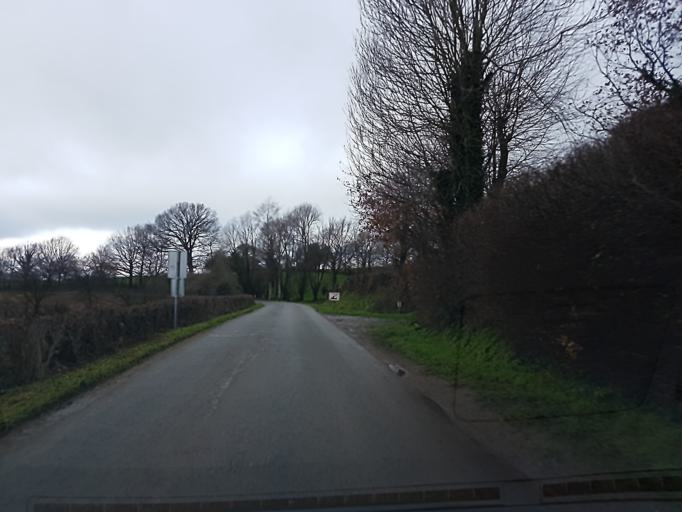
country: BE
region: Wallonia
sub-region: Province de Liege
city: Verviers
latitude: 50.5448
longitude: 5.8581
